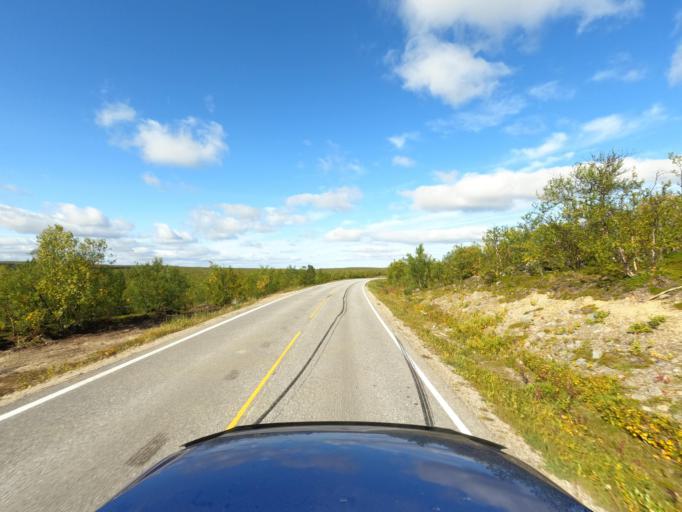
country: NO
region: Finnmark Fylke
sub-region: Karasjok
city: Karasjohka
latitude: 69.5308
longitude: 25.4390
